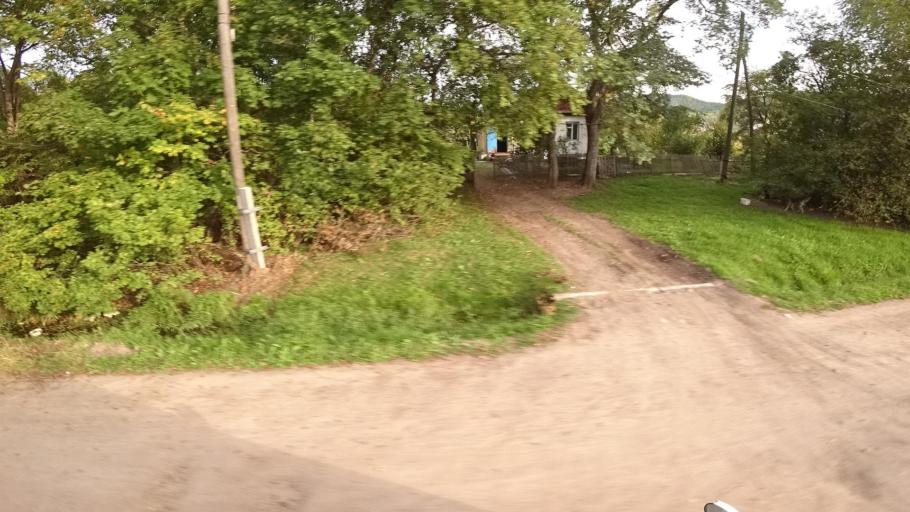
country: RU
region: Primorskiy
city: Yakovlevka
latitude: 44.4188
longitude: 133.4503
